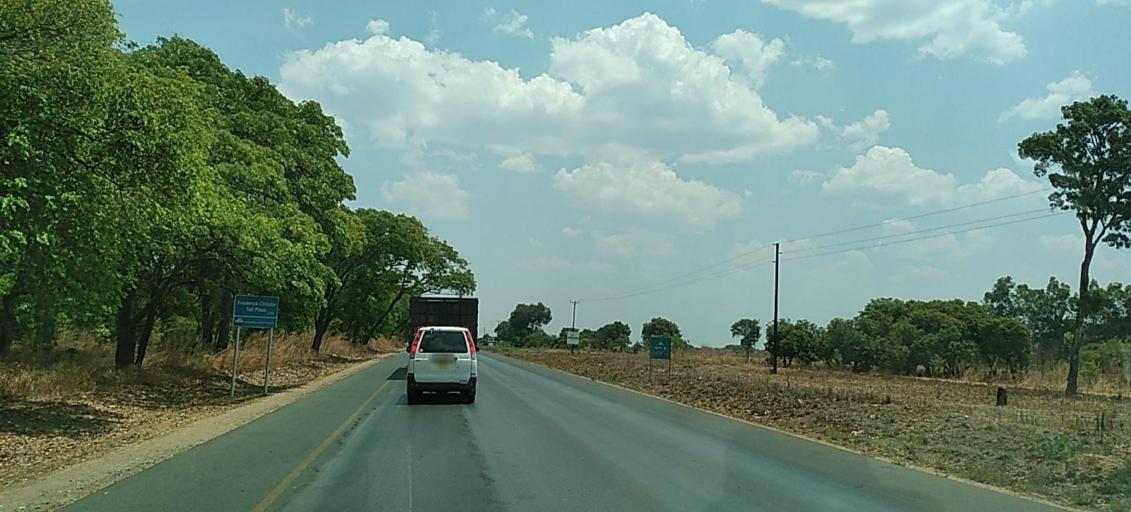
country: ZM
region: Central
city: Kabwe
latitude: -14.2318
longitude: 28.5717
